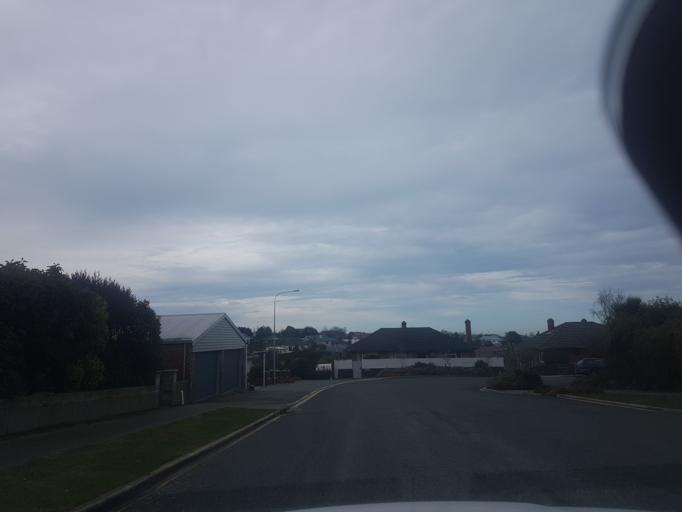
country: NZ
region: Canterbury
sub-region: Timaru District
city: Timaru
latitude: -44.4037
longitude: 171.2336
